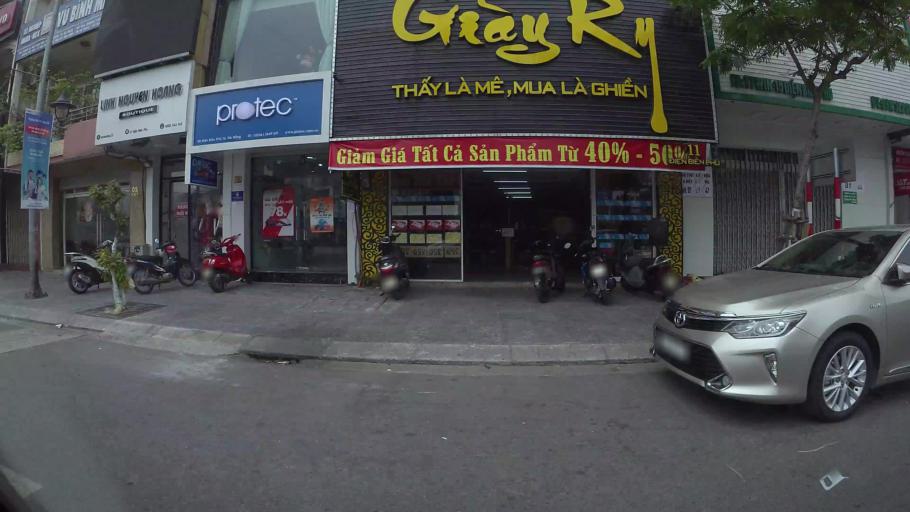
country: VN
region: Da Nang
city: Da Nang
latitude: 16.0658
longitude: 108.2065
